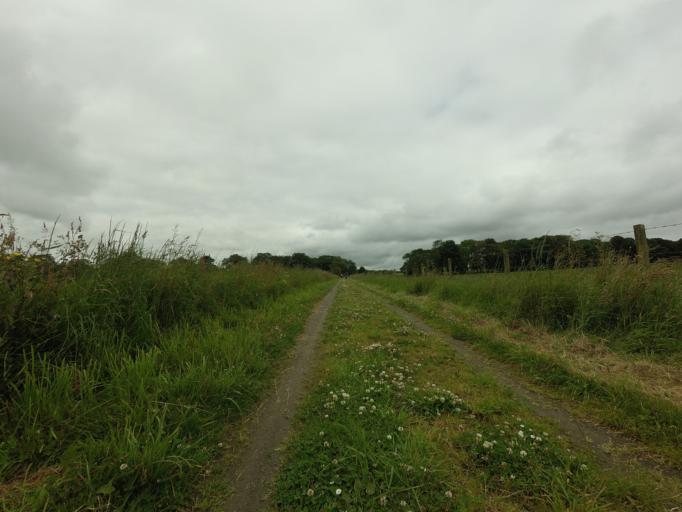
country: GB
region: Scotland
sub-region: Aberdeenshire
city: Ellon
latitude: 57.4858
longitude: -2.1351
